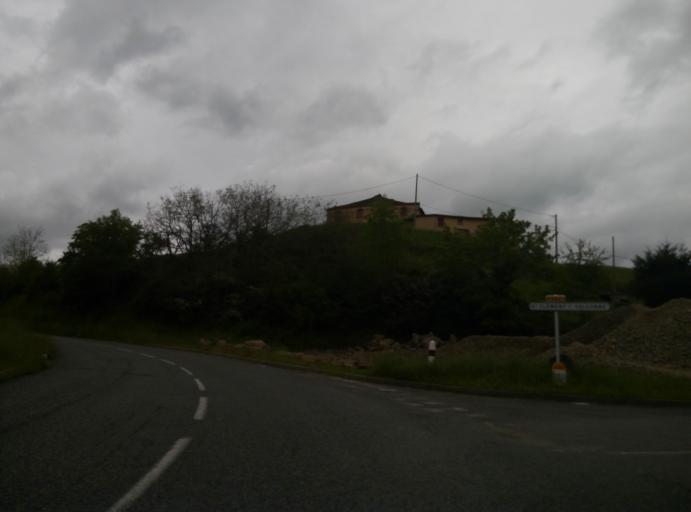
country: FR
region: Rhone-Alpes
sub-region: Departement du Rhone
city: Tarare
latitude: 45.9053
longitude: 4.4322
